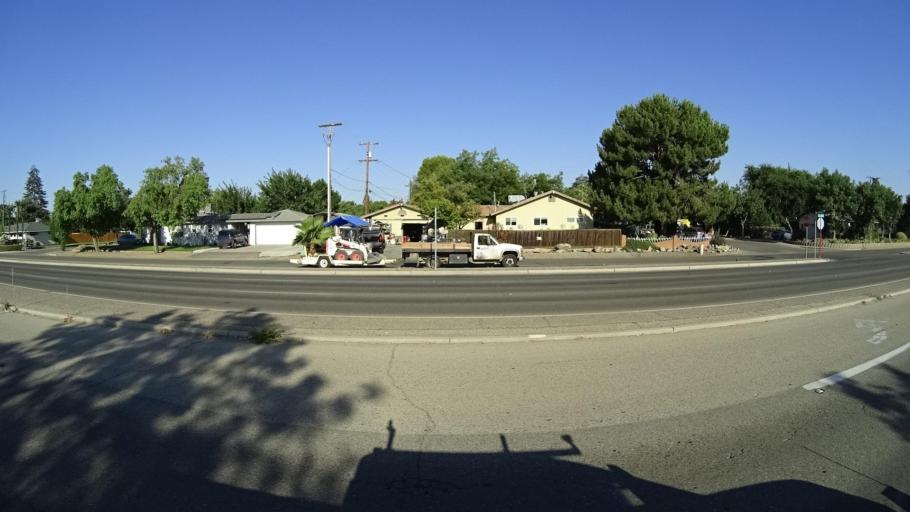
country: US
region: California
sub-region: Fresno County
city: Tarpey Village
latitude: 36.7892
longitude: -119.7010
